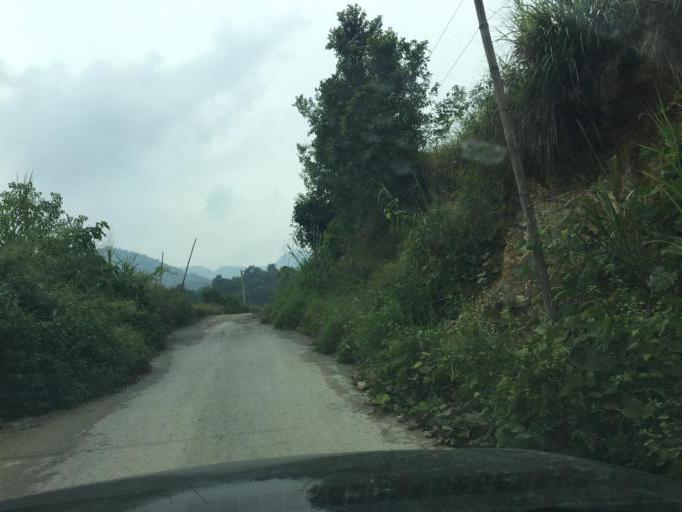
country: CN
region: Guangxi Zhuangzu Zizhiqu
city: Tongle
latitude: 25.1127
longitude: 106.2702
